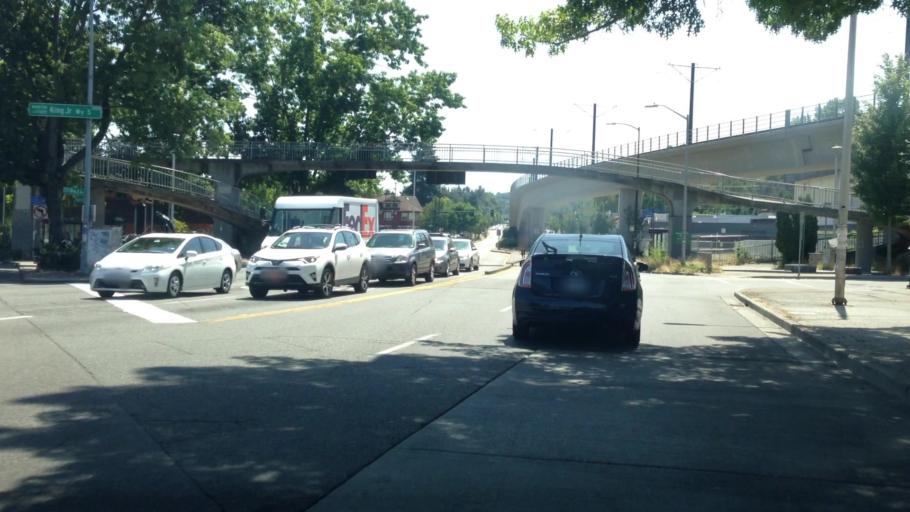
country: US
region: Washington
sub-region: King County
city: Seattle
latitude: 47.5763
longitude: -122.2968
